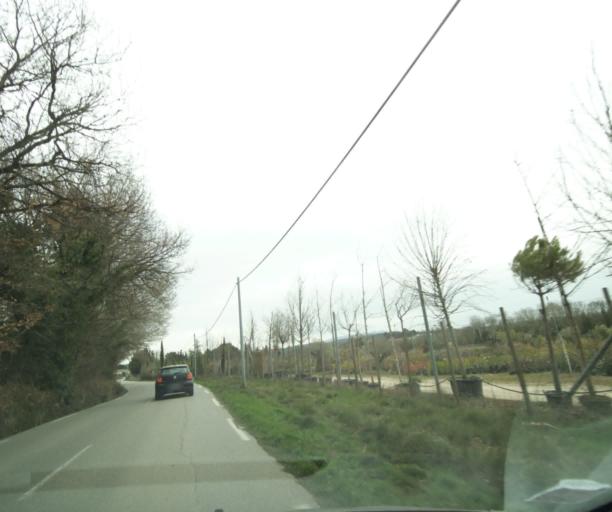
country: FR
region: Provence-Alpes-Cote d'Azur
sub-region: Departement des Bouches-du-Rhone
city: Venelles
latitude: 43.5813
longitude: 5.4608
